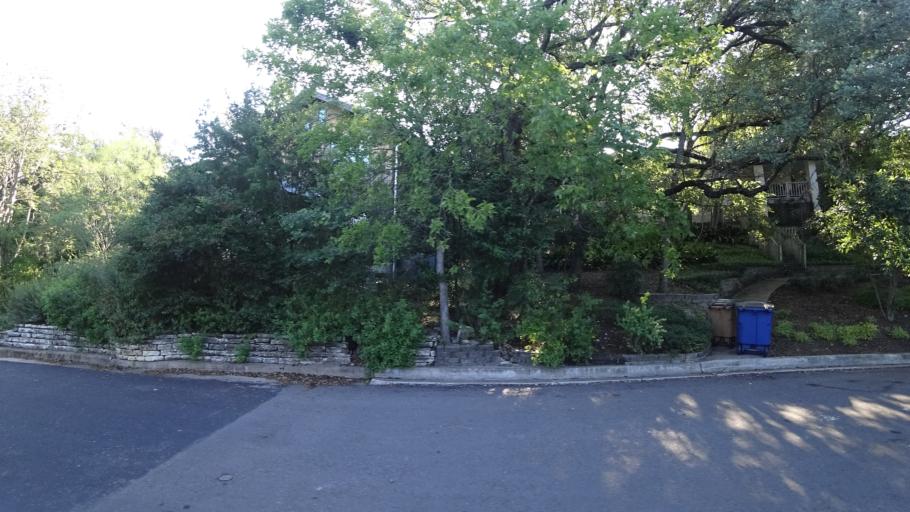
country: US
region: Texas
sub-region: Travis County
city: Austin
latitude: 30.2465
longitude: -97.7430
